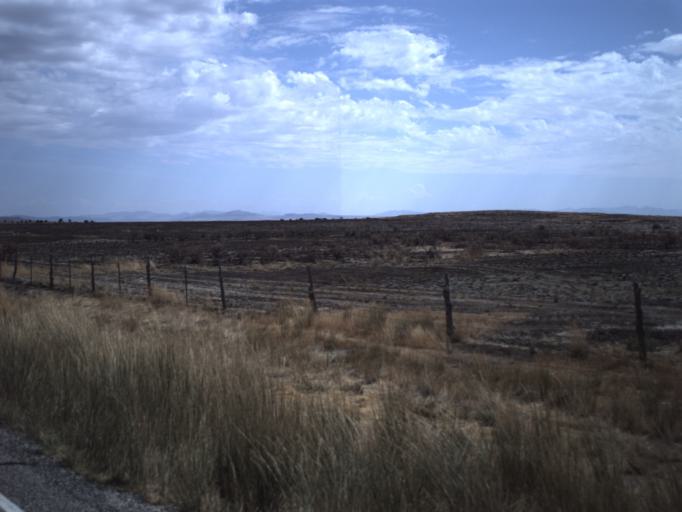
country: US
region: Idaho
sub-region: Minidoka County
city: Rupert
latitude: 41.8266
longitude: -113.1734
